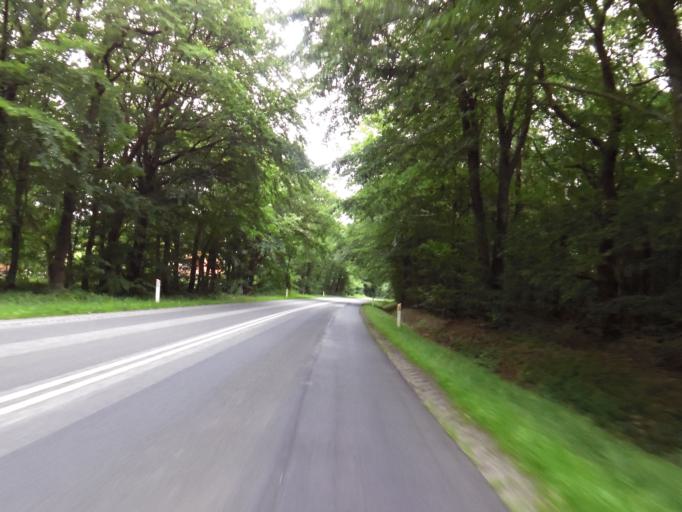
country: DK
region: South Denmark
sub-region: Tonder Kommune
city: Toftlund
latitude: 55.1870
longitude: 8.9594
